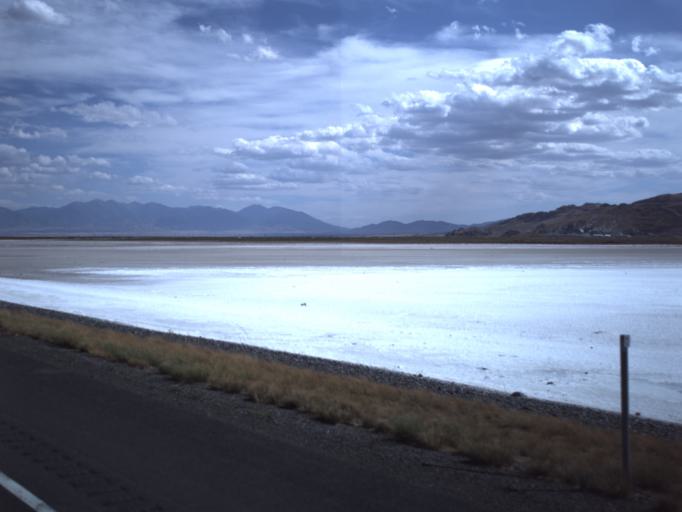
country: US
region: Utah
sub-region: Tooele County
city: Grantsville
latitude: 40.7287
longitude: -112.5851
